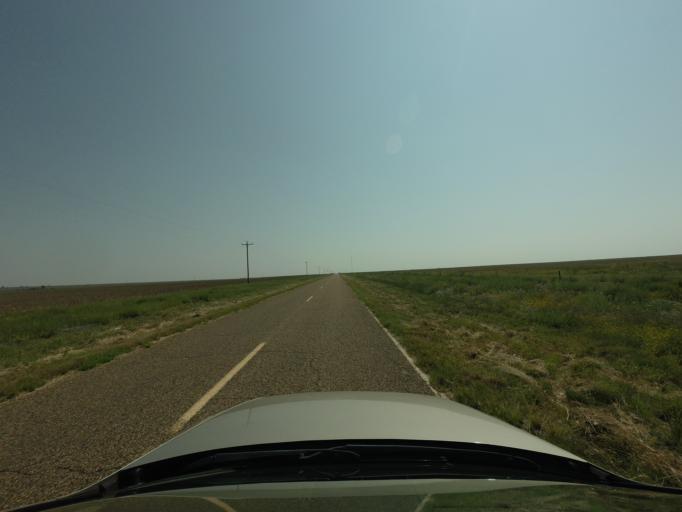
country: US
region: New Mexico
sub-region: Curry County
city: Cannon Air Force Base
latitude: 34.6336
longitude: -103.6153
